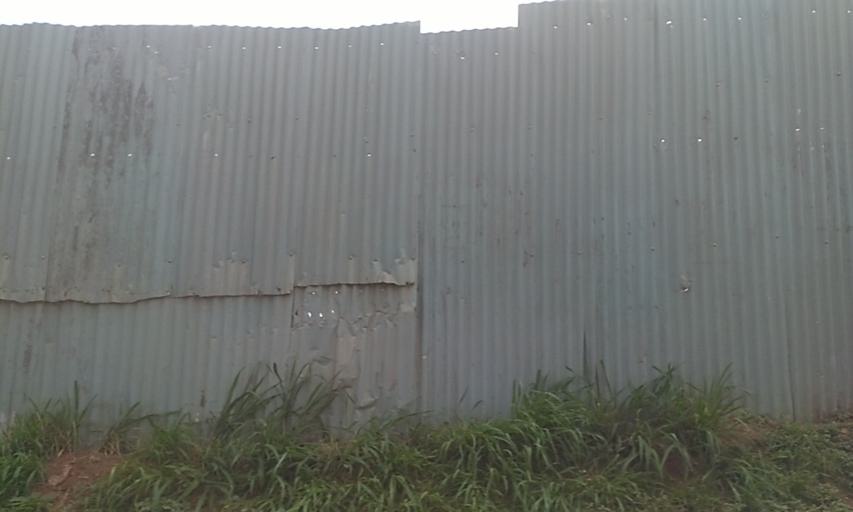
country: UG
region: Central Region
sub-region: Kampala District
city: Kampala
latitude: 0.3351
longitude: 32.6101
